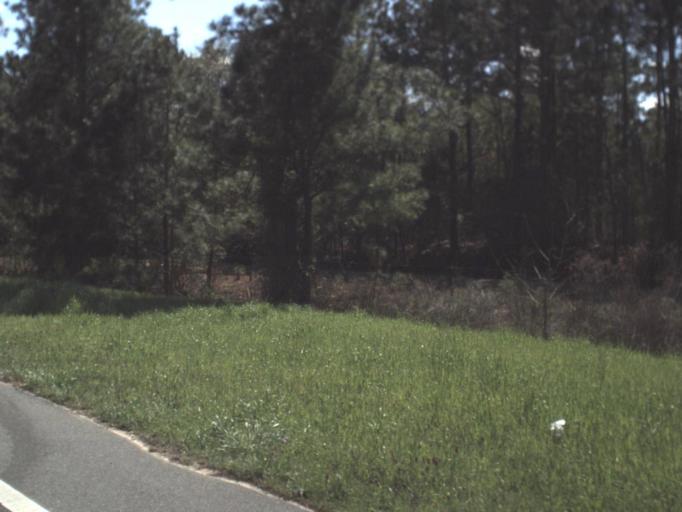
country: US
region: Florida
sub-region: Gadsden County
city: Gretna
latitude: 30.6326
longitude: -84.6721
